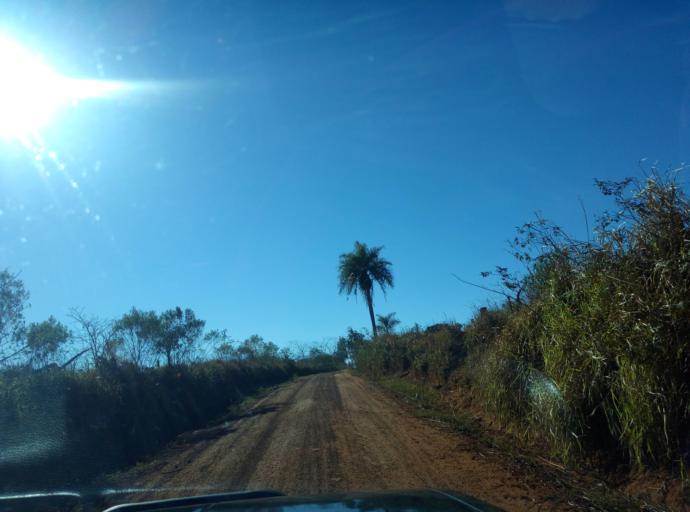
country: PY
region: Caaguazu
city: Doctor Cecilio Baez
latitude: -25.1647
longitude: -56.2339
